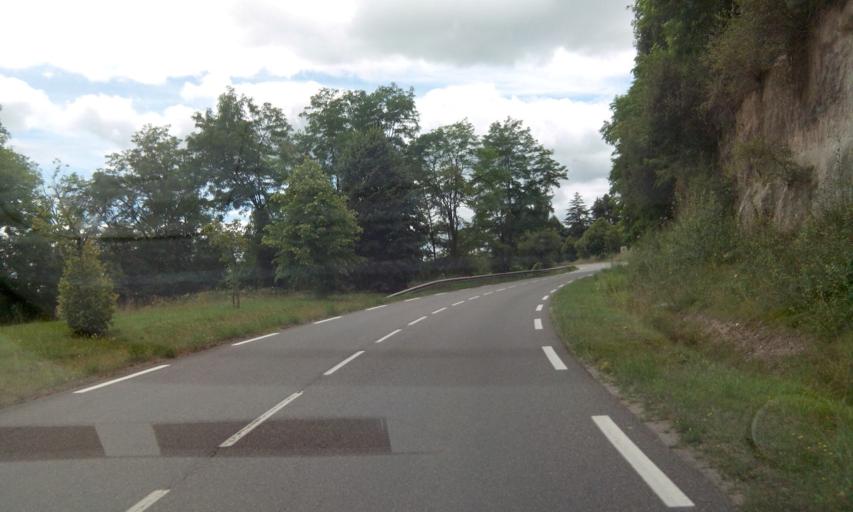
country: FR
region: Limousin
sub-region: Departement de la Correze
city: Brive-la-Gaillarde
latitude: 45.1272
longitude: 1.5542
